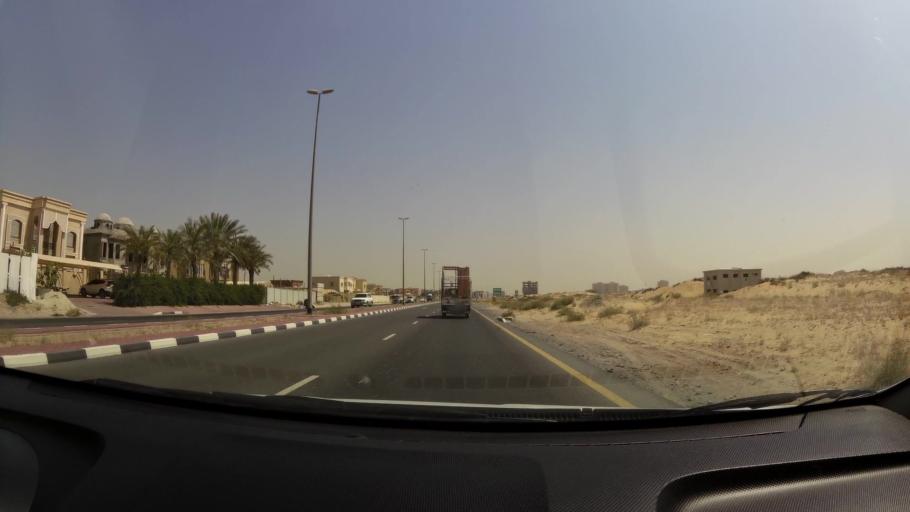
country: AE
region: Ajman
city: Ajman
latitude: 25.4172
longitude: 55.5288
